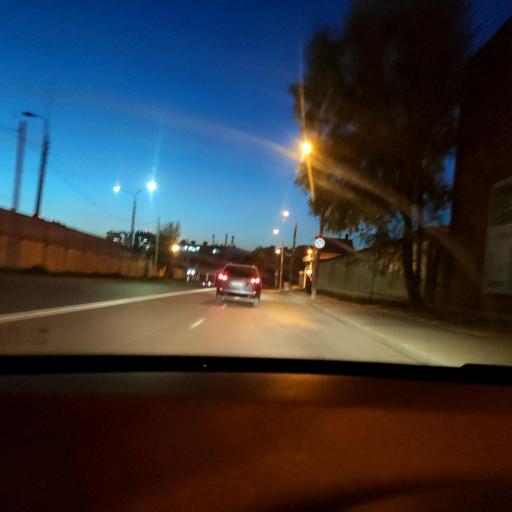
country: RU
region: Samara
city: Samara
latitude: 53.1850
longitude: 50.1482
